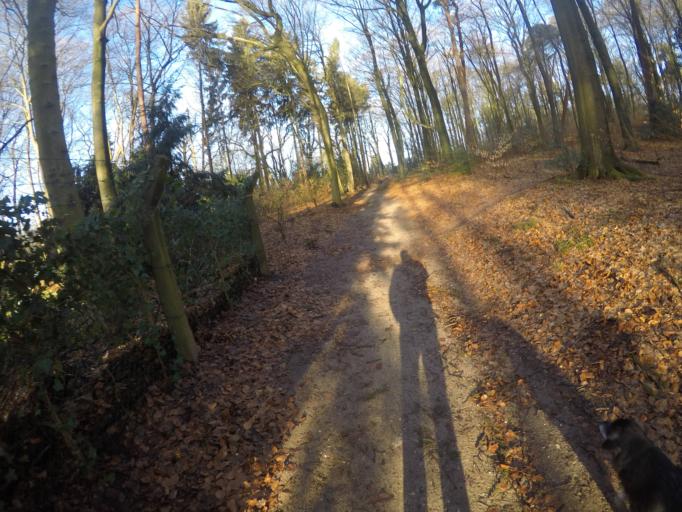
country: NL
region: Gelderland
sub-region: Gemeente Arnhem
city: Gulden Bodem
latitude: 51.9969
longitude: 5.8877
